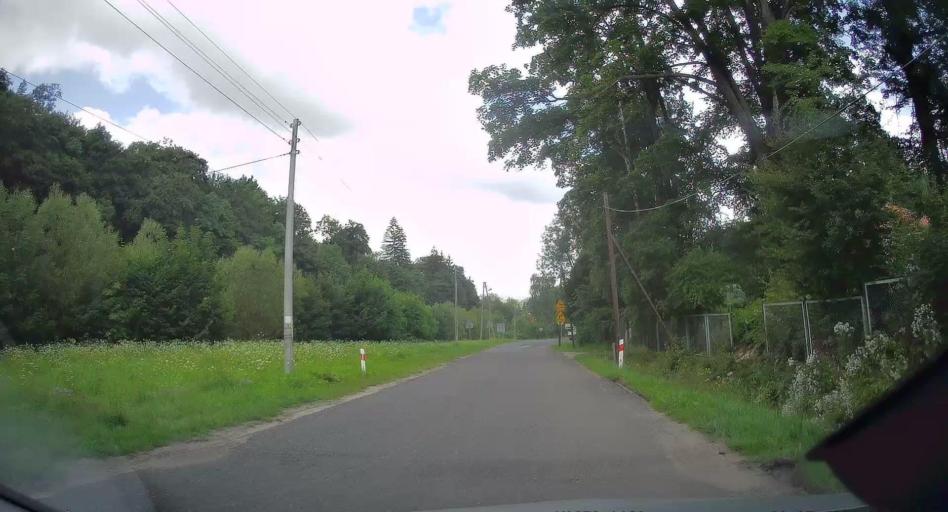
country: PL
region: Lower Silesian Voivodeship
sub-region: Powiat walbrzyski
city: Walim
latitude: 50.7219
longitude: 16.4152
